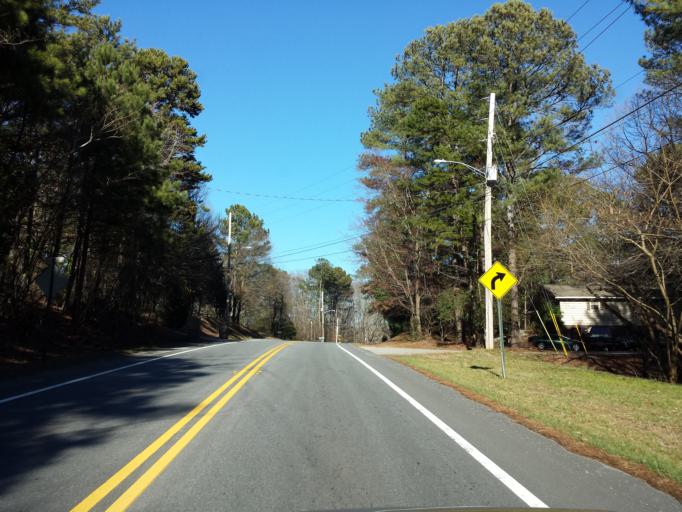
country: US
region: Georgia
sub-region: Cobb County
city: Kennesaw
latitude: 33.9669
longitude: -84.6407
